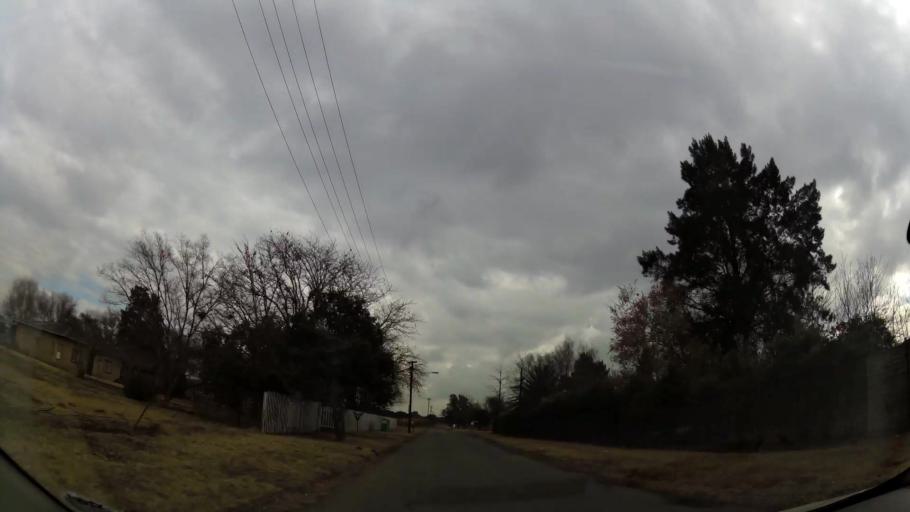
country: ZA
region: Gauteng
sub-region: Sedibeng District Municipality
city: Meyerton
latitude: -26.5834
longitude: 28.0002
